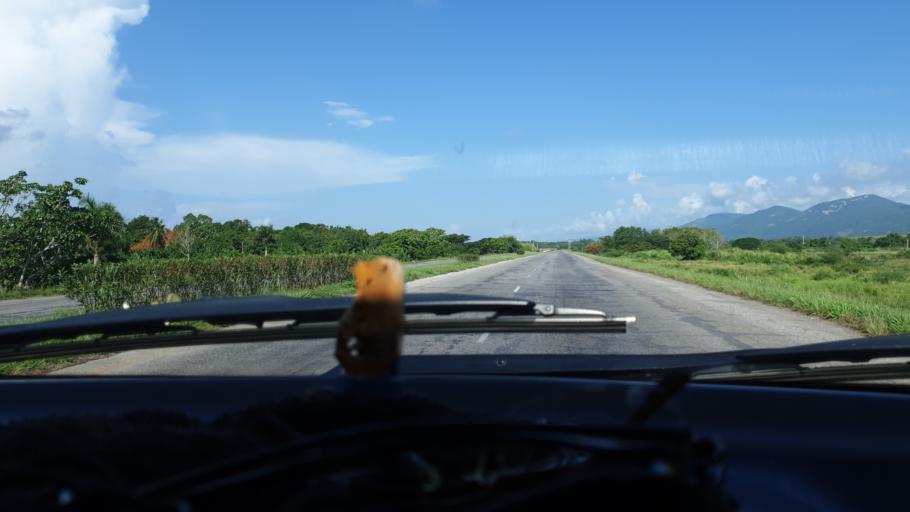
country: CU
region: Artemisa
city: San Cristobal
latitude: 22.7226
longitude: -83.0383
